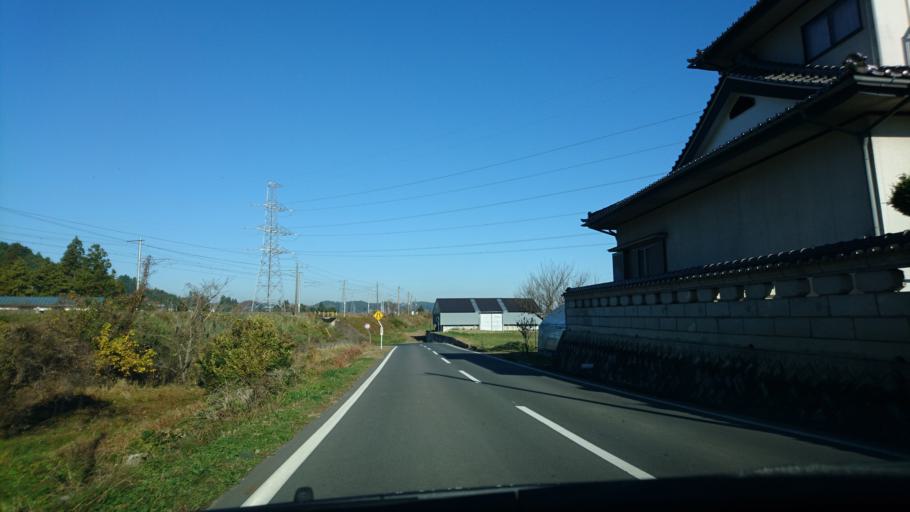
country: JP
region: Iwate
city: Ichinoseki
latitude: 39.0240
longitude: 141.1304
